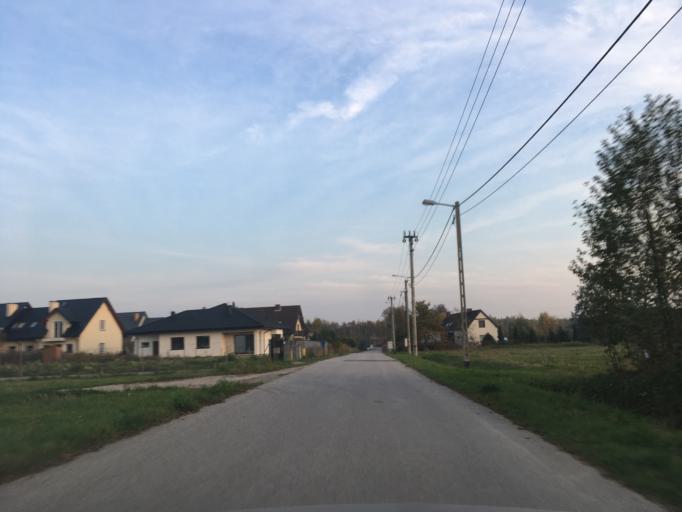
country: PL
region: Masovian Voivodeship
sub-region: Powiat piaseczynski
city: Lesznowola
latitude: 52.0489
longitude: 20.9283
